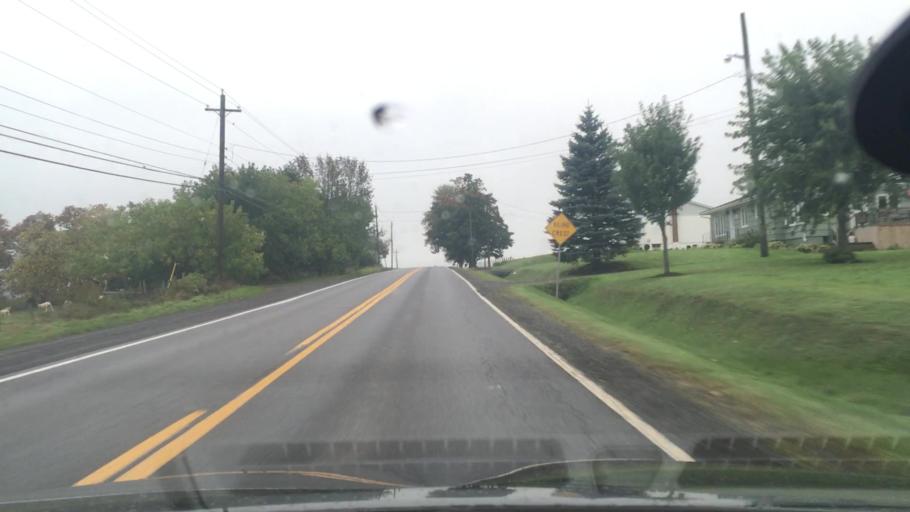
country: CA
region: Nova Scotia
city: Windsor
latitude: 44.9691
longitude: -64.1421
